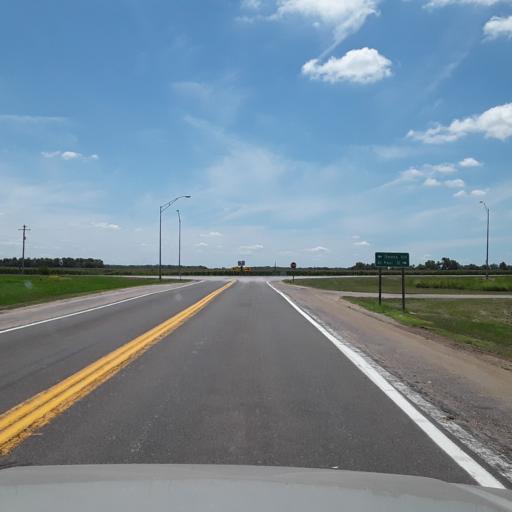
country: US
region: Nebraska
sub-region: Merrick County
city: Central City
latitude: 41.1924
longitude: -97.8723
